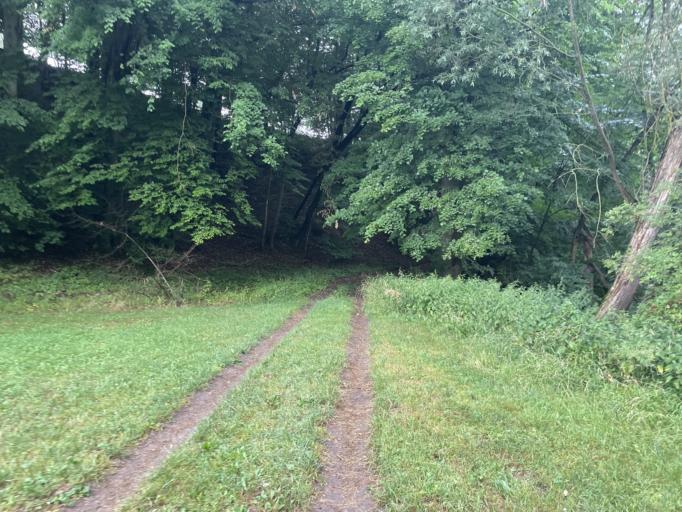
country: DE
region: Bavaria
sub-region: Upper Franconia
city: Neunkirchen am Main
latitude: 49.9335
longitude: 11.6343
